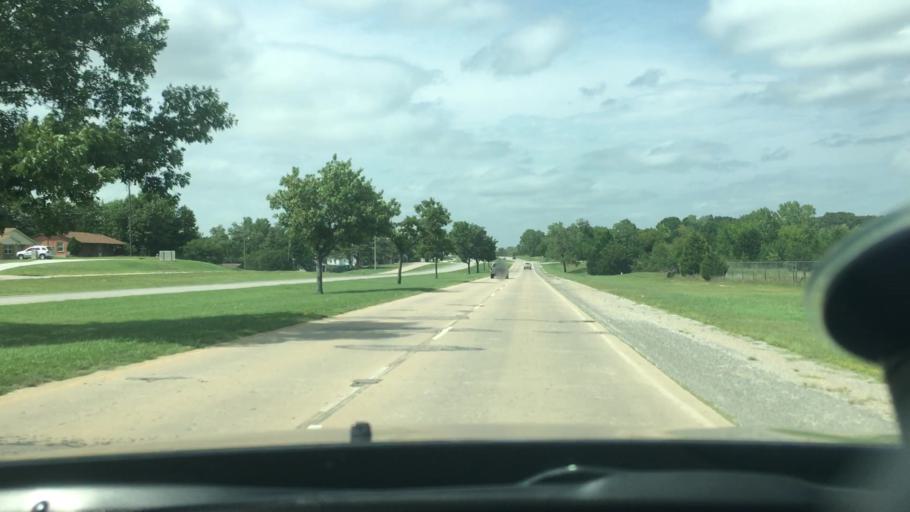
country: US
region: Oklahoma
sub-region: Pontotoc County
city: Ada
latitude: 34.8076
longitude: -96.6782
